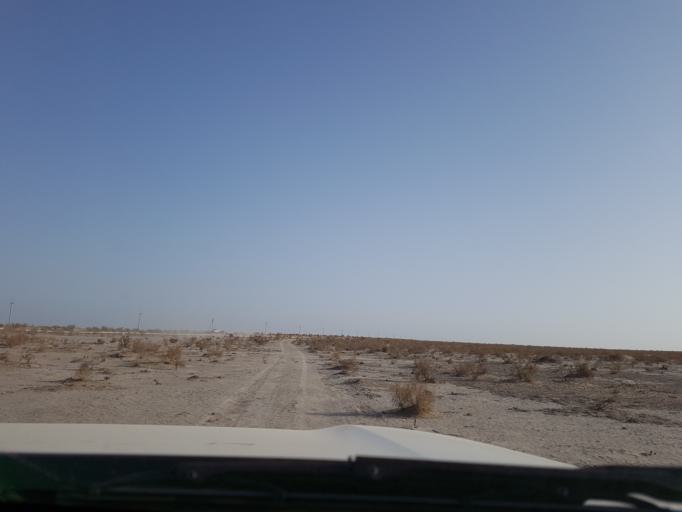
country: UZ
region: Karakalpakstan
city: Shumanay Shahri
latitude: 42.0098
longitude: 58.0970
